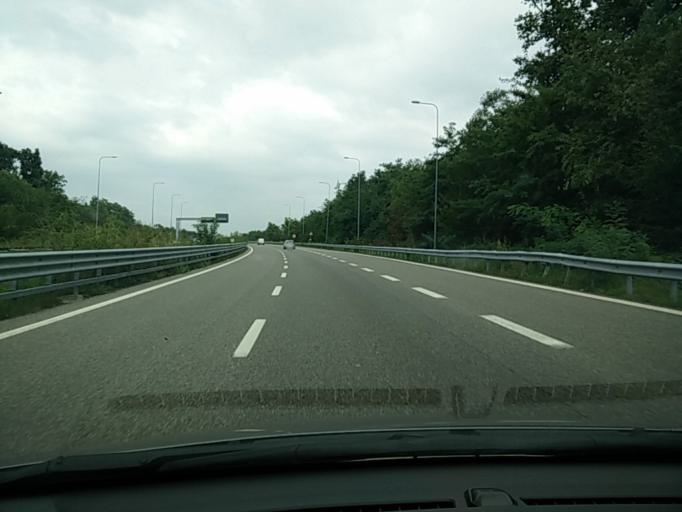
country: IT
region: Lombardy
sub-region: Provincia di Varese
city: Lonate Pozzolo
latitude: 45.5710
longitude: 8.7466
